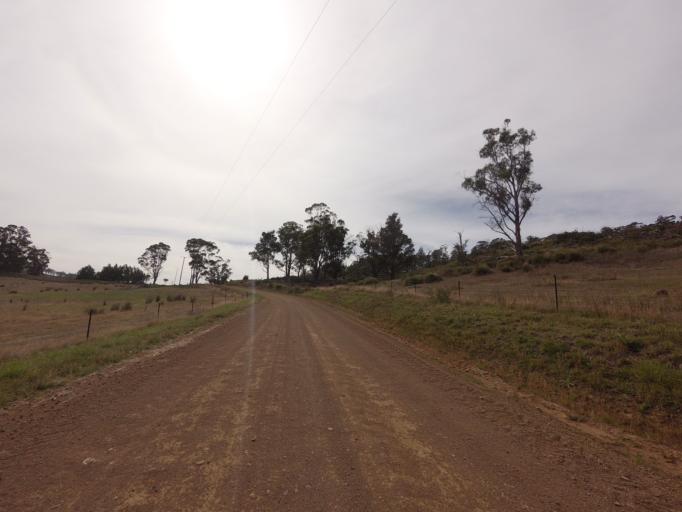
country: AU
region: Tasmania
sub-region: Sorell
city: Sorell
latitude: -42.4808
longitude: 147.5837
